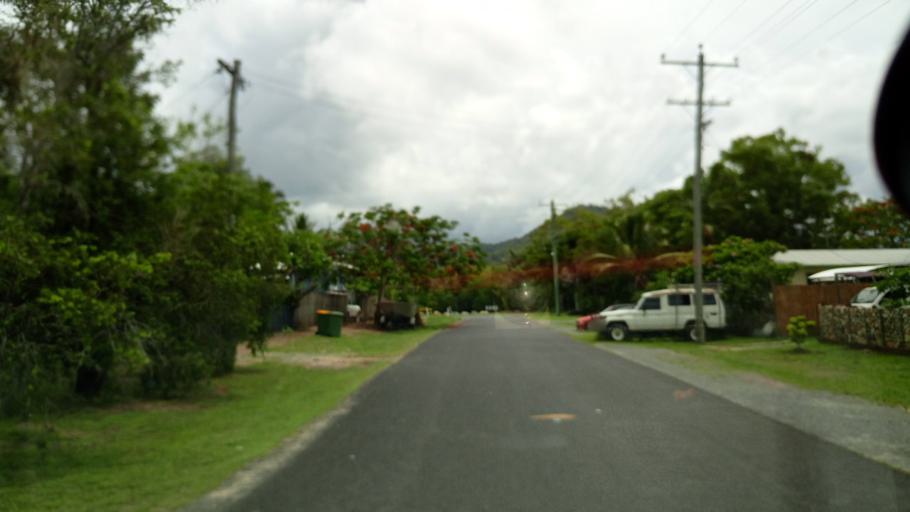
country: AU
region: Queensland
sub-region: Cairns
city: Redlynch
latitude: -16.8591
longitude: 145.7450
